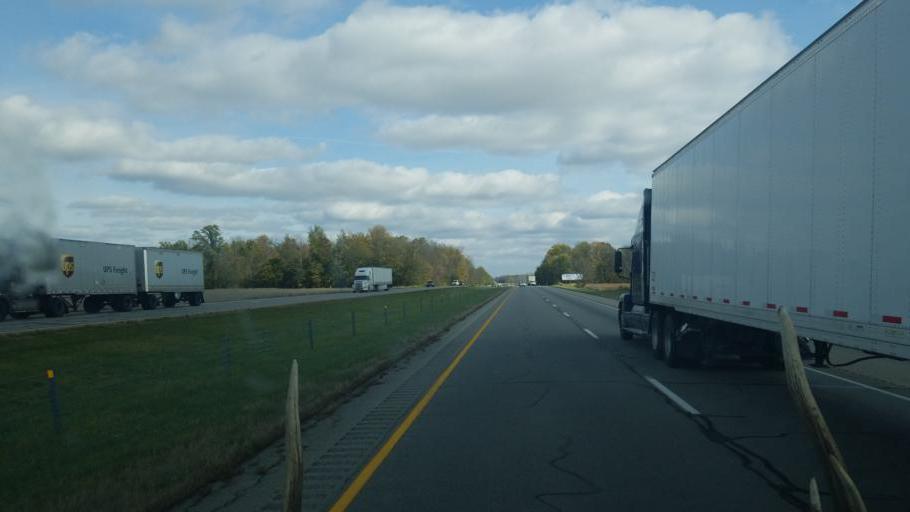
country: US
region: Indiana
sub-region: Henry County
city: New Castle
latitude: 39.8526
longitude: -85.3735
